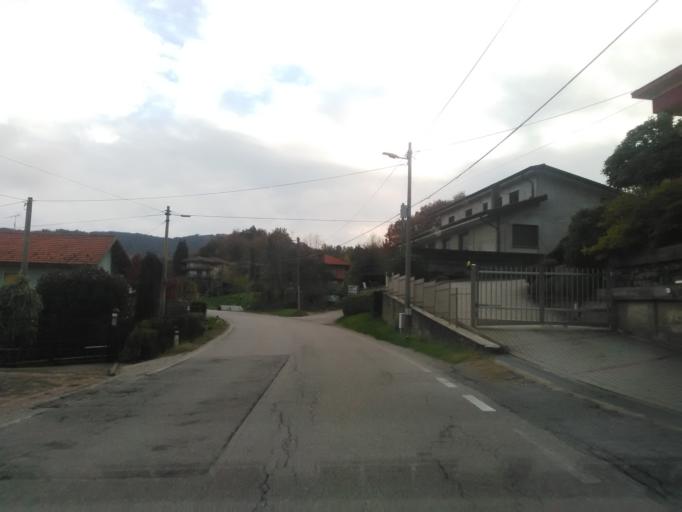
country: IT
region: Piedmont
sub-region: Provincia di Novara
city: Pogno
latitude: 45.7549
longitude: 8.3803
